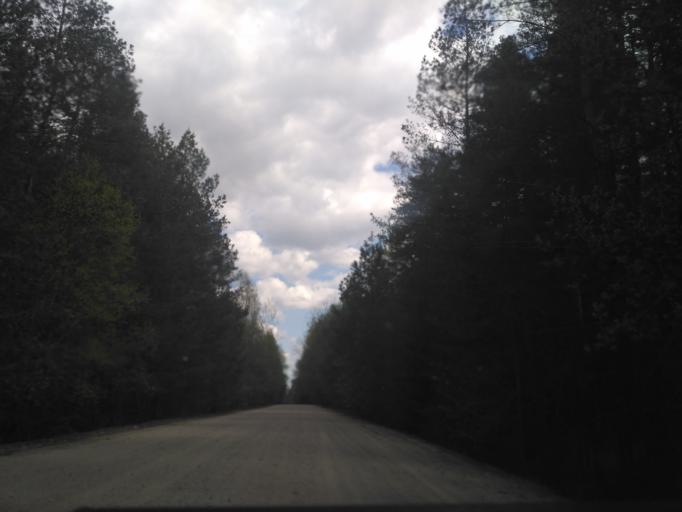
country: BY
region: Minsk
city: Radashkovichy
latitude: 54.2662
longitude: 27.3037
